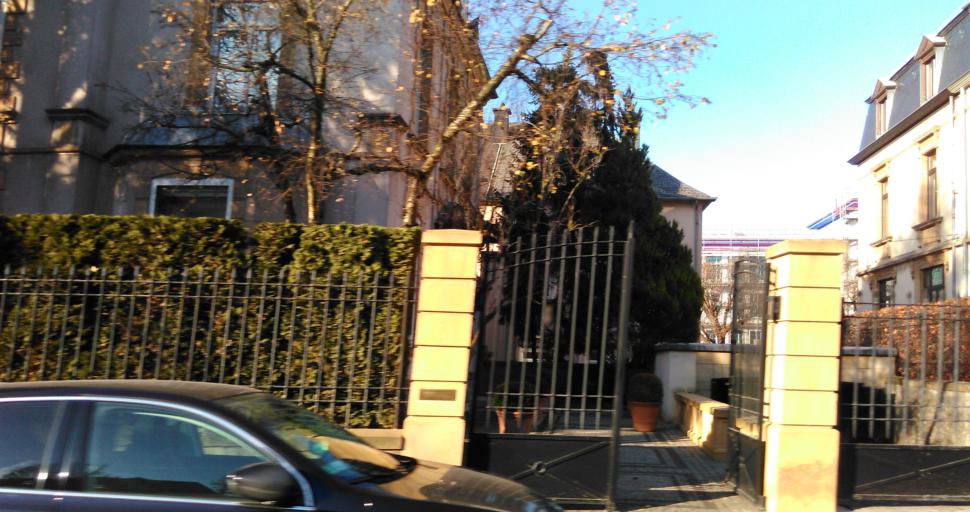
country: LU
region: Luxembourg
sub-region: Canton de Luxembourg
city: Luxembourg
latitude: 49.6143
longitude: 6.1217
